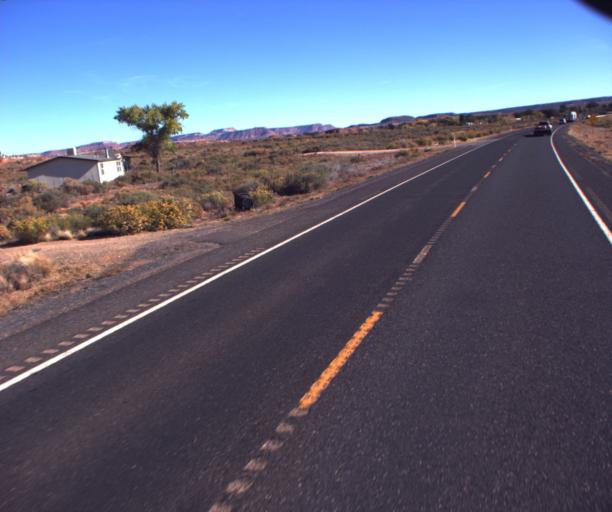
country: US
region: Arizona
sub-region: Coconino County
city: Fredonia
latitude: 36.9443
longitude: -112.5413
